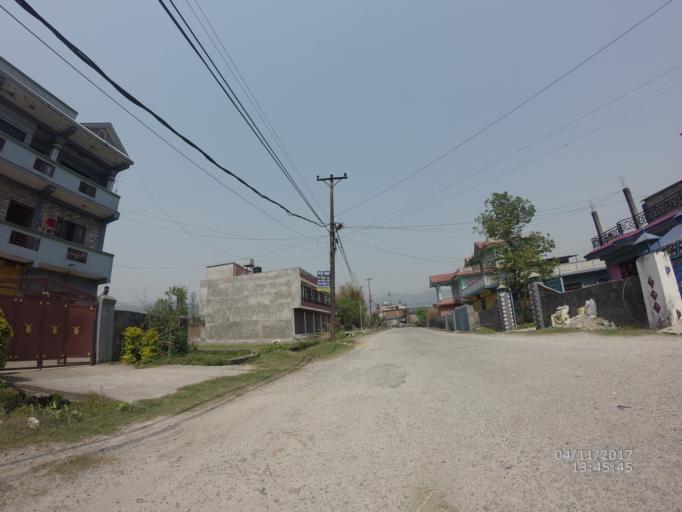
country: NP
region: Western Region
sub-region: Gandaki Zone
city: Pokhara
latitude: 28.1823
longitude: 84.0363
